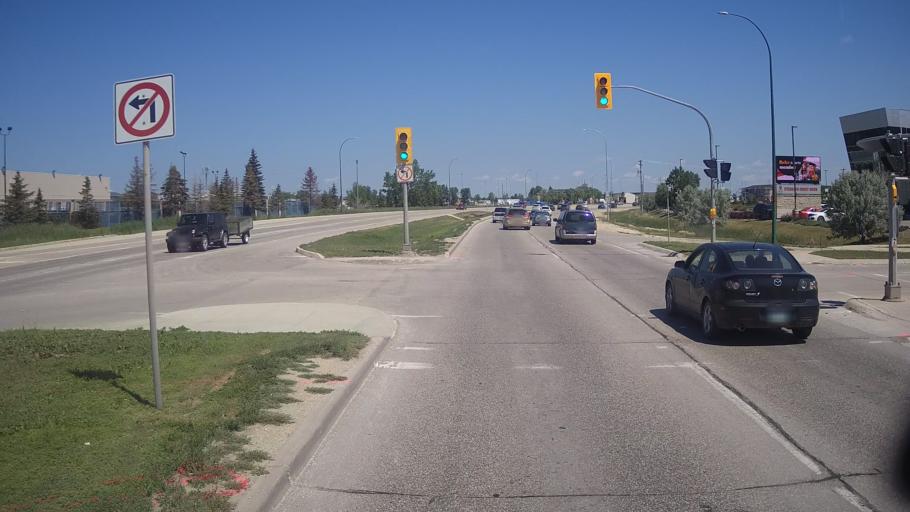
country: CA
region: Manitoba
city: Winnipeg
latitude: 49.9046
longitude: -97.0645
